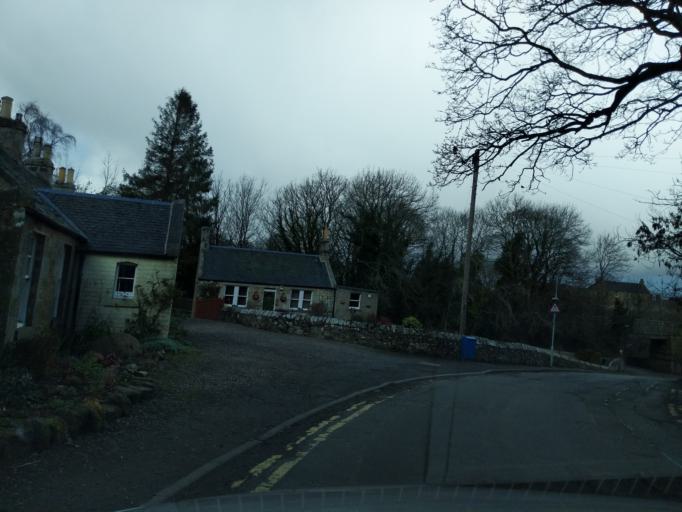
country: GB
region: Scotland
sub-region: Edinburgh
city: Currie
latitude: 55.8950
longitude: -3.3089
